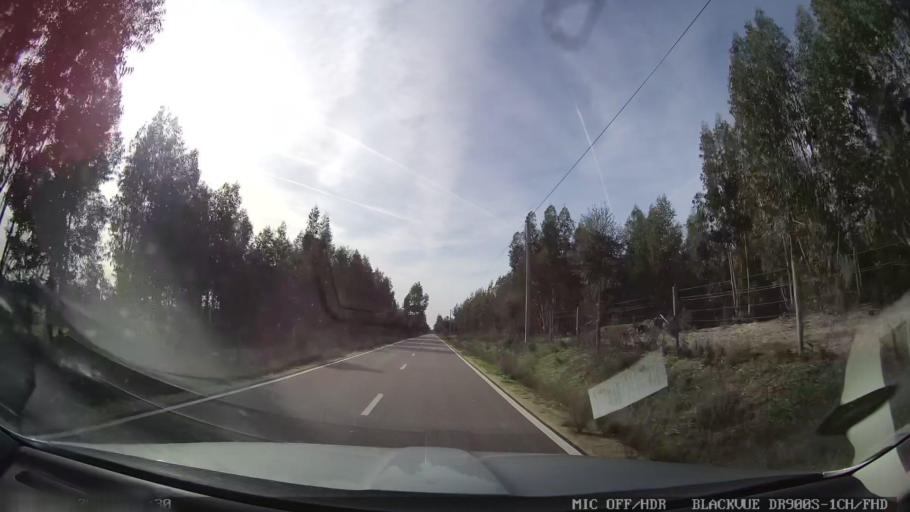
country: PT
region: Portalegre
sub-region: Nisa
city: Nisa
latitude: 39.4615
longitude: -7.7028
